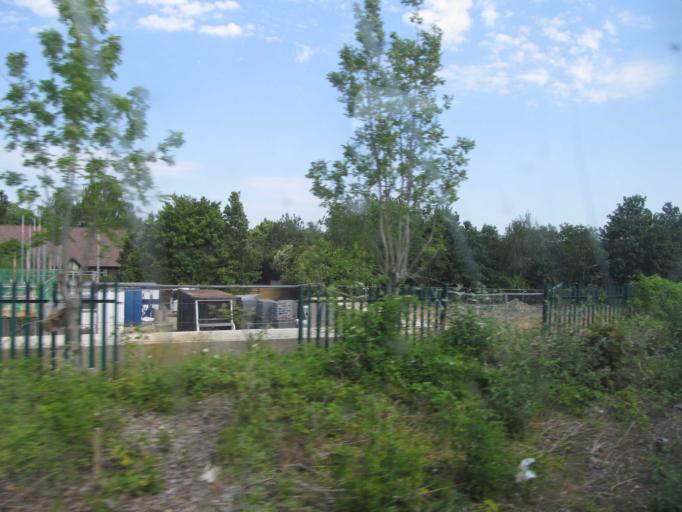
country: GB
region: England
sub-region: Royal Borough of Windsor and Maidenhead
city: Bray
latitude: 51.5236
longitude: -0.6798
